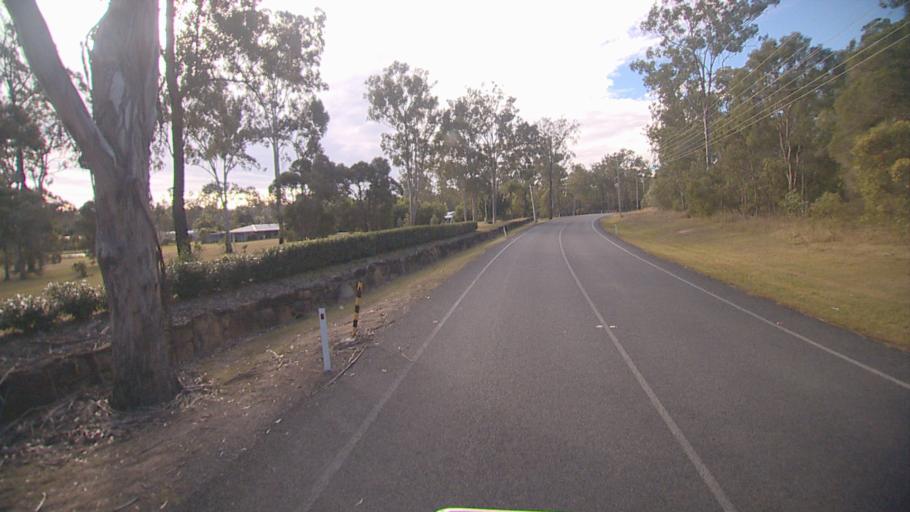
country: AU
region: Queensland
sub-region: Logan
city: North Maclean
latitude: -27.8132
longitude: 153.0565
